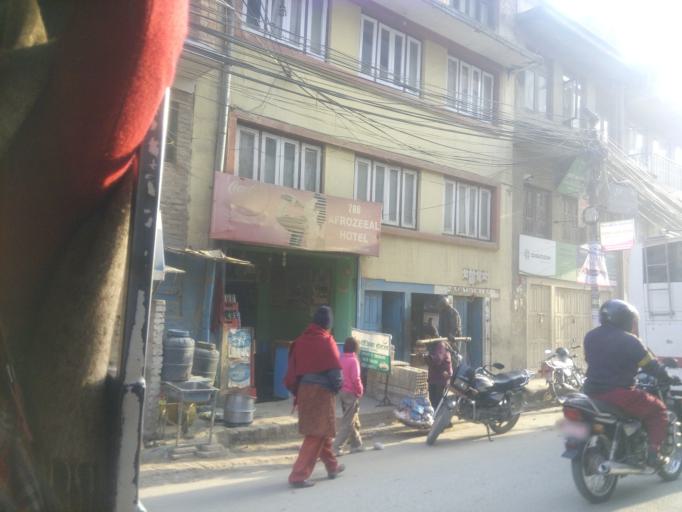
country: NP
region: Central Region
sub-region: Bagmati Zone
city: Patan
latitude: 27.6685
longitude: 85.3255
